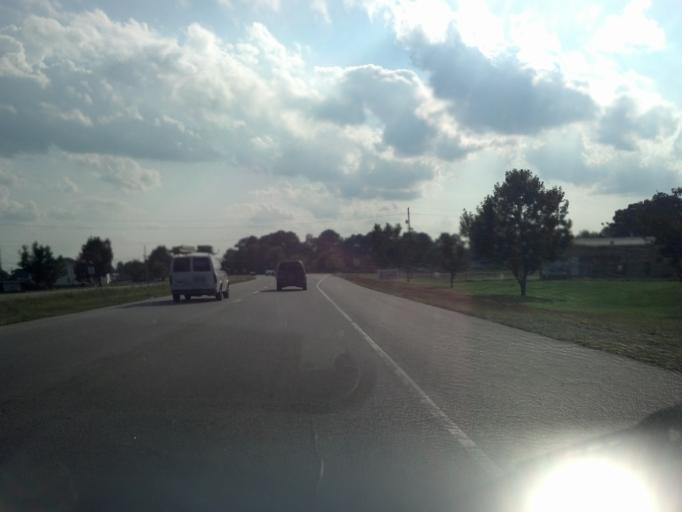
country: US
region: North Carolina
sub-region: Pitt County
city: Greenville
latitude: 35.6372
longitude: -77.3745
